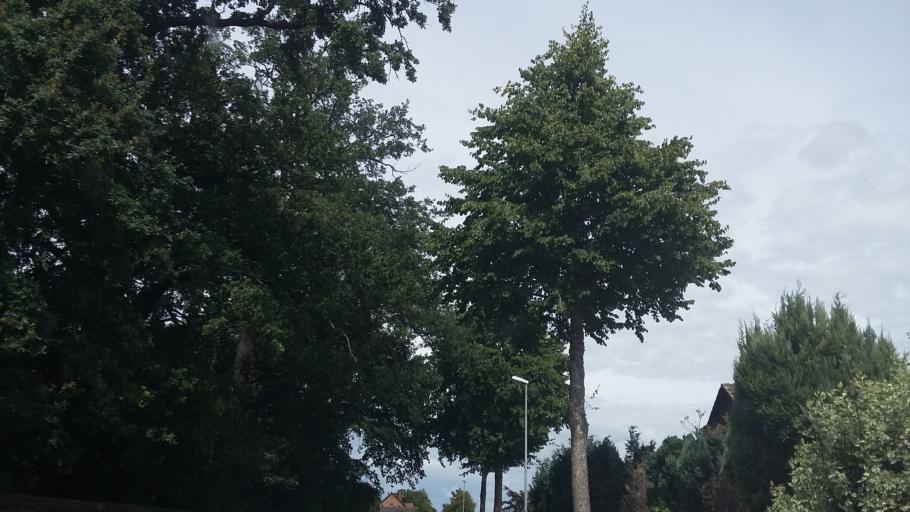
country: DE
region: Lower Saxony
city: Harsum
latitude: 52.1865
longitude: 10.0083
